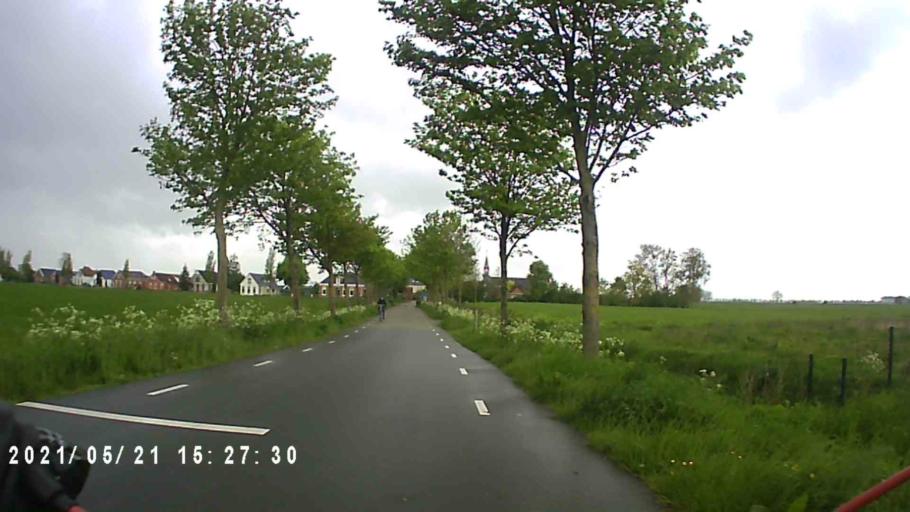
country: NL
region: Groningen
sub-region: Gemeente Zuidhorn
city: Aduard
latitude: 53.2290
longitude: 6.4517
